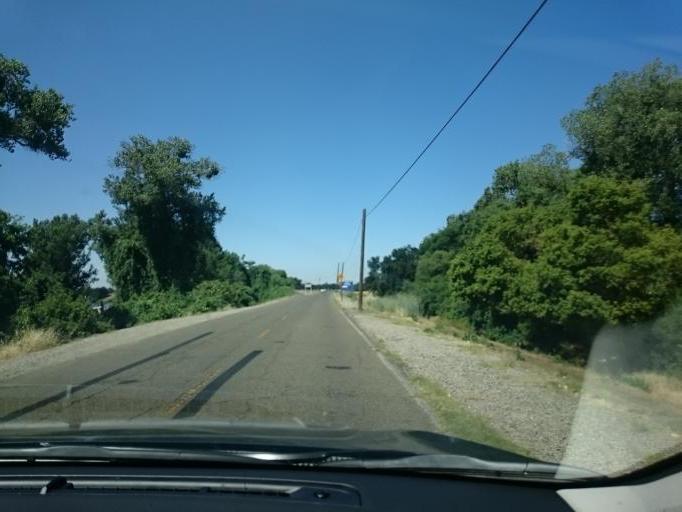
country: US
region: California
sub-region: Yolo County
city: West Sacramento
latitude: 38.5341
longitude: -121.5266
